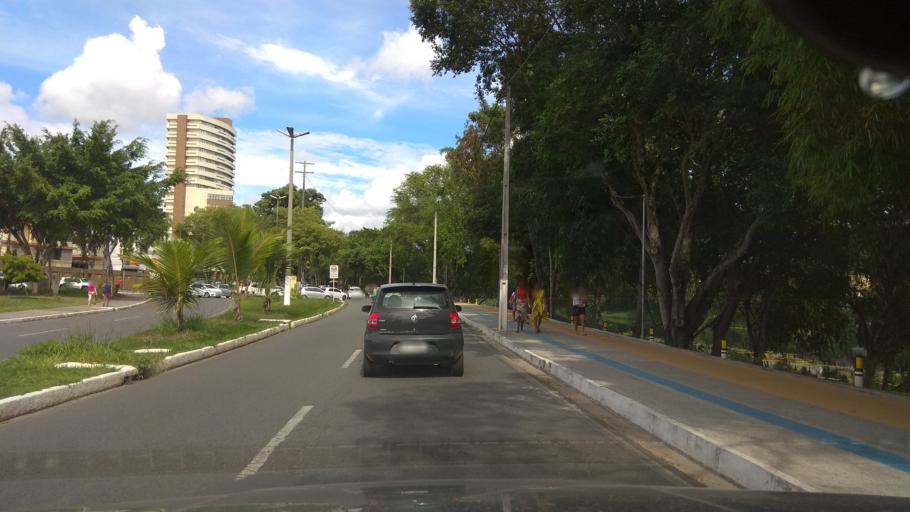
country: BR
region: Bahia
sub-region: Itabuna
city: Itabuna
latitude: -14.7949
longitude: -39.2743
